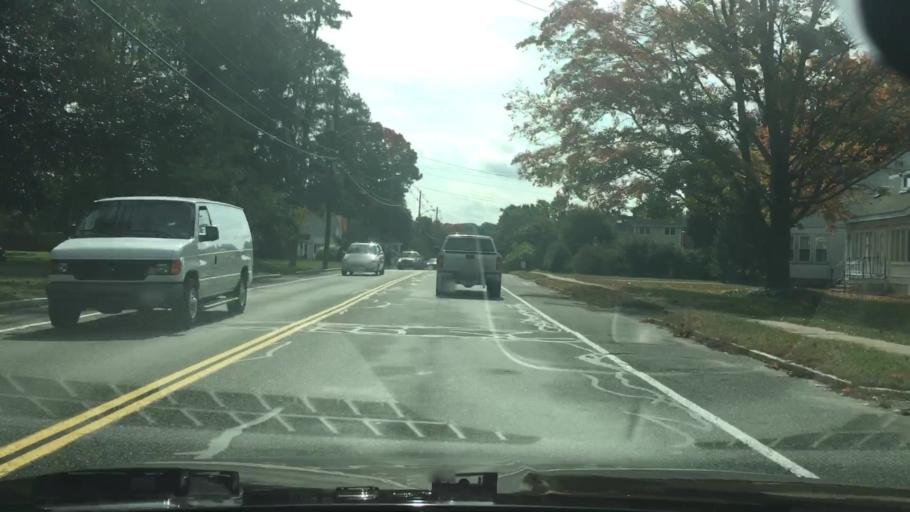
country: US
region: Massachusetts
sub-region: Hampden County
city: East Longmeadow
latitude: 42.0697
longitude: -72.5159
